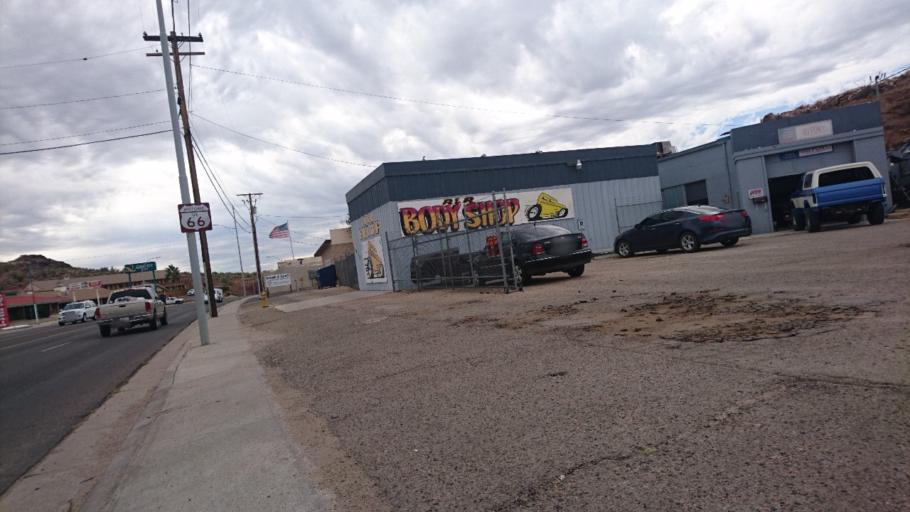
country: US
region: Arizona
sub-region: Mohave County
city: Kingman
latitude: 35.1920
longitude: -114.0345
